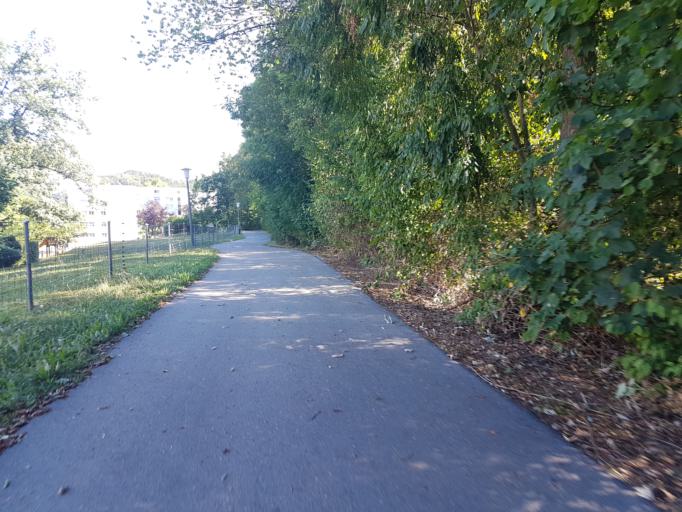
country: CH
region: Zurich
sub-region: Bezirk Pfaeffikon
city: Effretikon / Rappenhalde-Bannhalde
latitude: 47.4245
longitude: 8.6946
